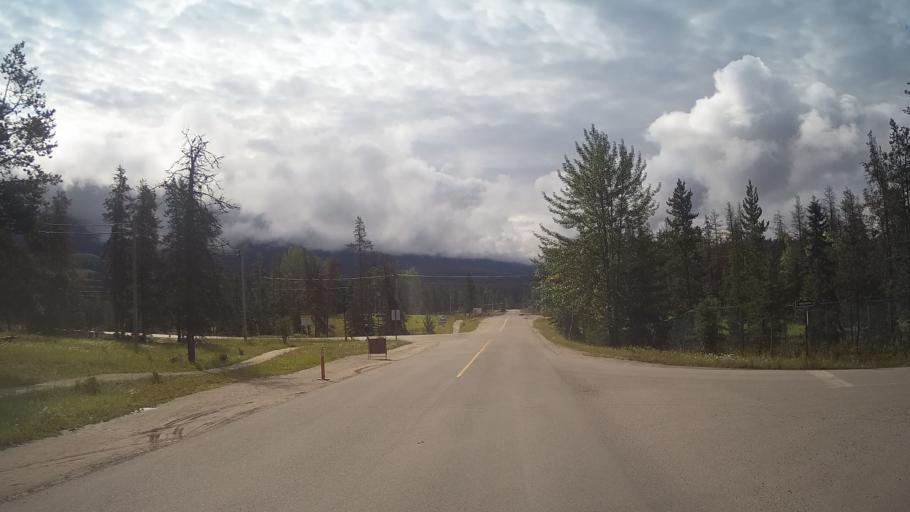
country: CA
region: Alberta
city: Jasper Park Lodge
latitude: 52.8715
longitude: -118.0799
